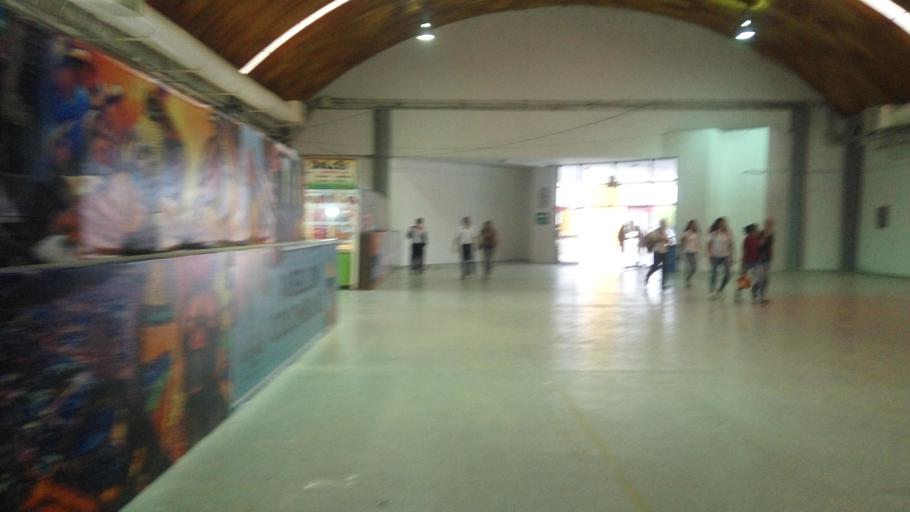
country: MX
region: Tabasco
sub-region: Nacajuca
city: Bosque de Saloya
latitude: 18.0066
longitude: -92.9634
